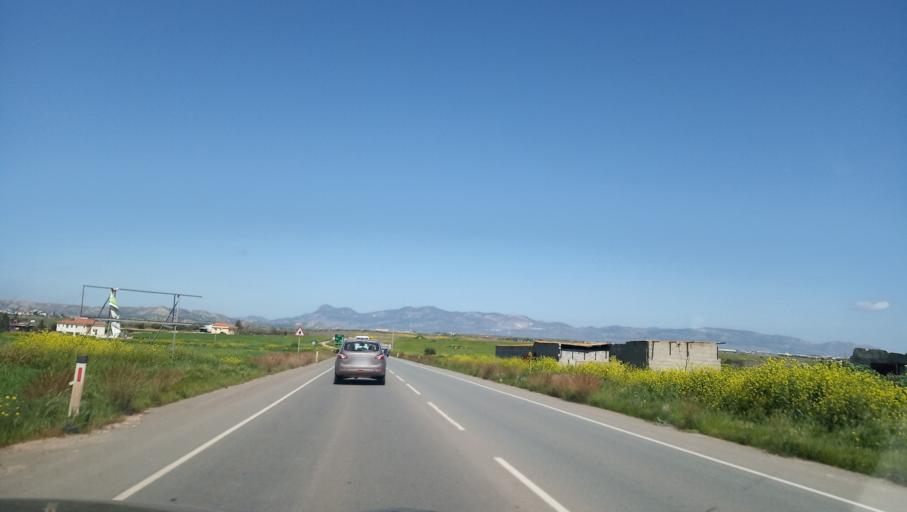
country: CY
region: Lefkosia
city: Akaki
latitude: 35.1498
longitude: 33.1555
